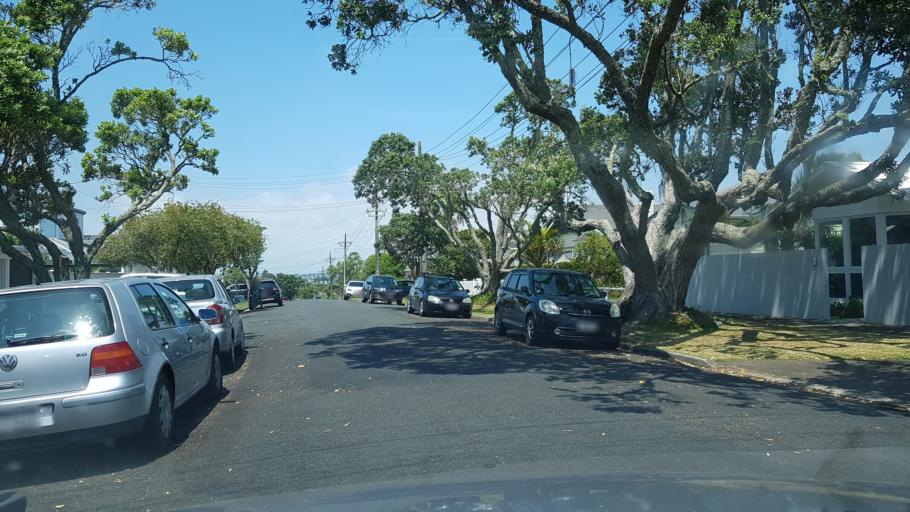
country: NZ
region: Auckland
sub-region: Auckland
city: North Shore
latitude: -36.8099
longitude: 174.7960
